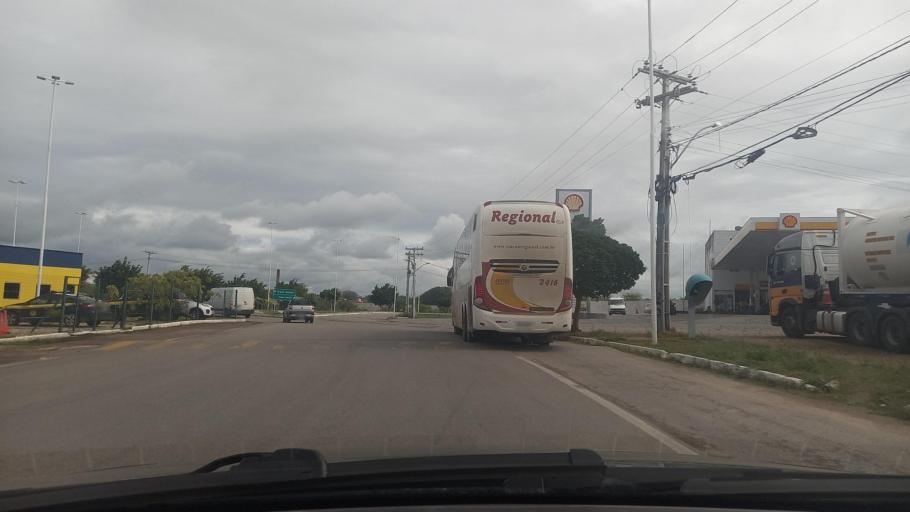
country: BR
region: Bahia
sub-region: Paulo Afonso
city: Paulo Afonso
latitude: -9.4374
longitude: -38.2043
